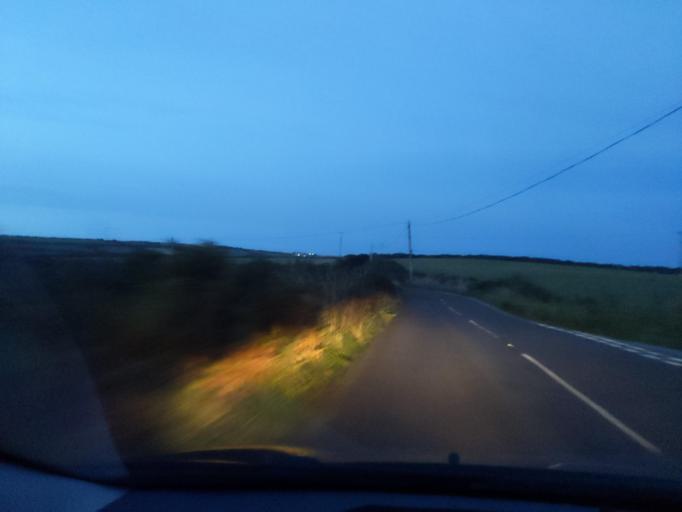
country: GB
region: England
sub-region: Cornwall
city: Camelford
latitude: 50.6955
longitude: -4.6693
